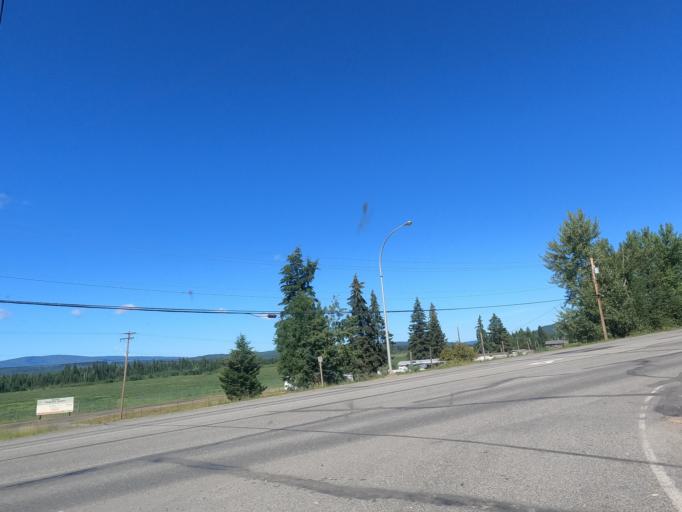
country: CA
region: British Columbia
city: Quesnel
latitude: 53.0157
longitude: -122.4950
